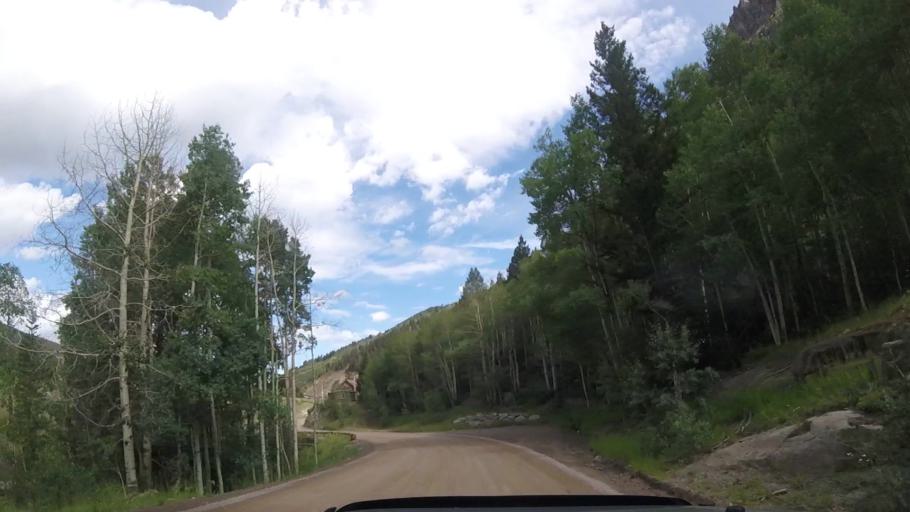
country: US
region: Colorado
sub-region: San Miguel County
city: Mountain Village
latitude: 37.8603
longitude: -107.8686
